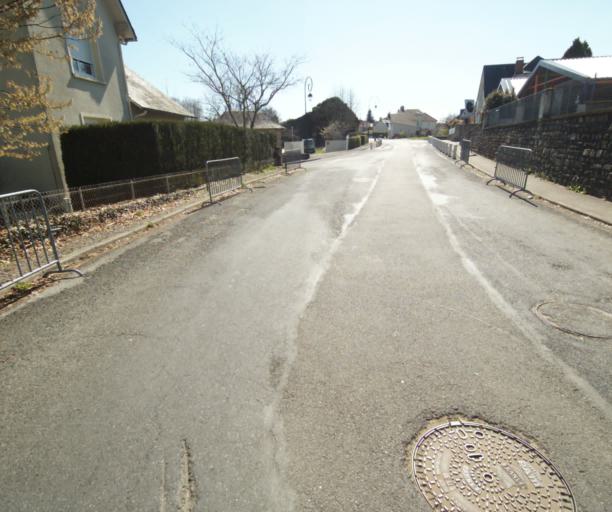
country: FR
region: Limousin
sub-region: Departement de la Correze
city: Saint-Mexant
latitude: 45.2857
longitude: 1.6584
